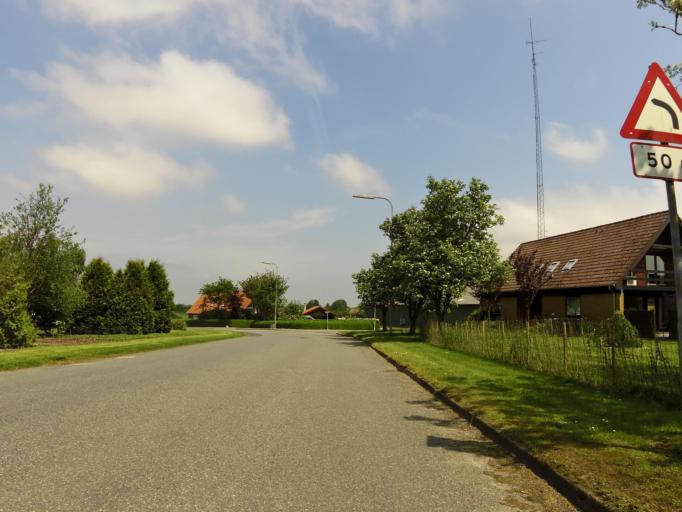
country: DK
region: South Denmark
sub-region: Tonder Kommune
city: Toftlund
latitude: 55.1927
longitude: 9.0793
